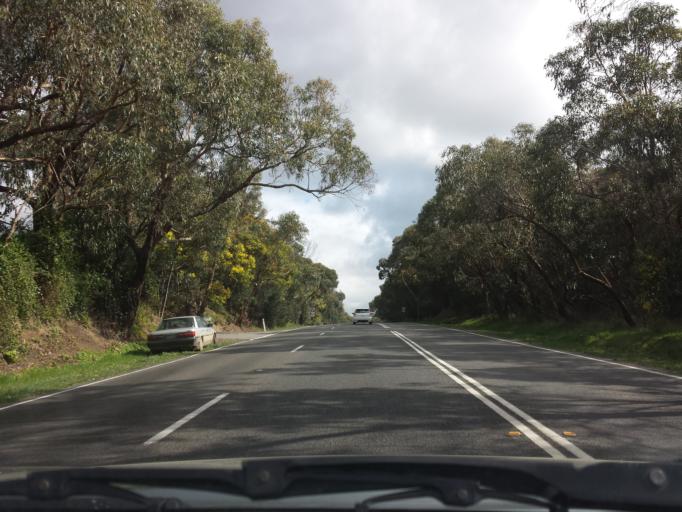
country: AU
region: Victoria
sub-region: Yarra Ranges
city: Belgrave South
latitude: -37.9525
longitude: 145.3432
